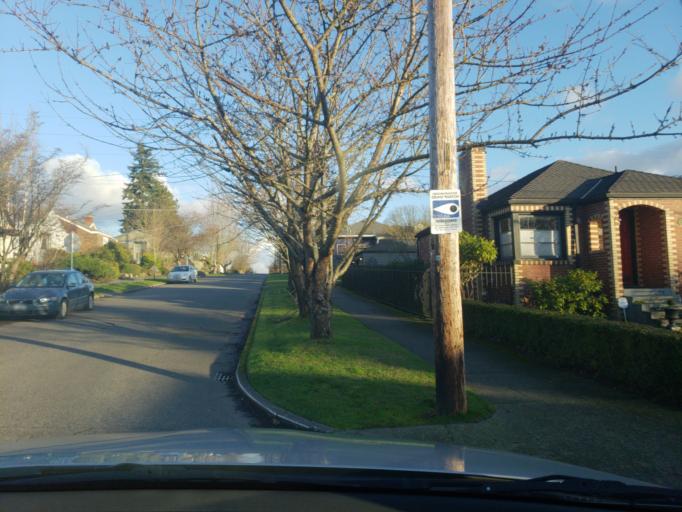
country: US
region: Washington
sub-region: King County
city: Shoreline
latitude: 47.6833
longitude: -122.3714
